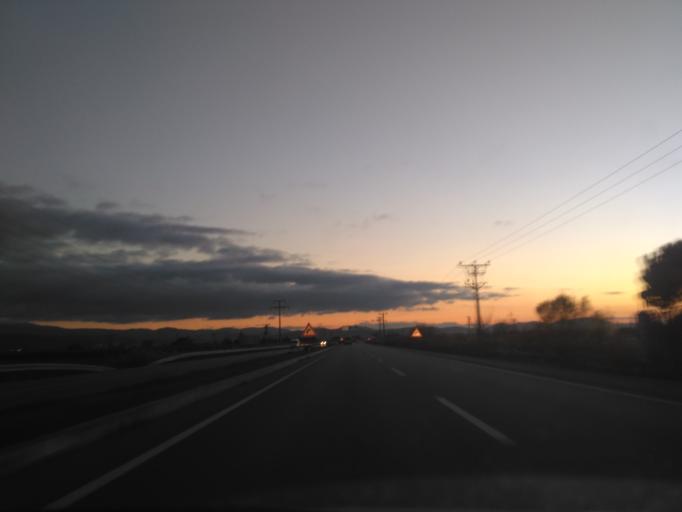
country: TR
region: Balikesir
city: Burhaniye
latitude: 39.5310
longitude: 27.0071
